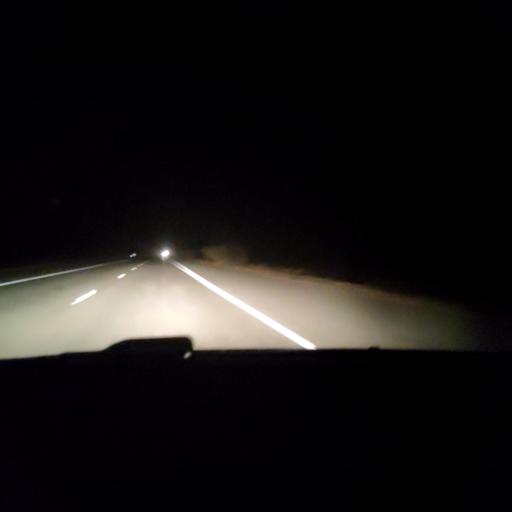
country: RU
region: Voronezj
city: Strelitsa
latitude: 51.5008
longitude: 38.9652
